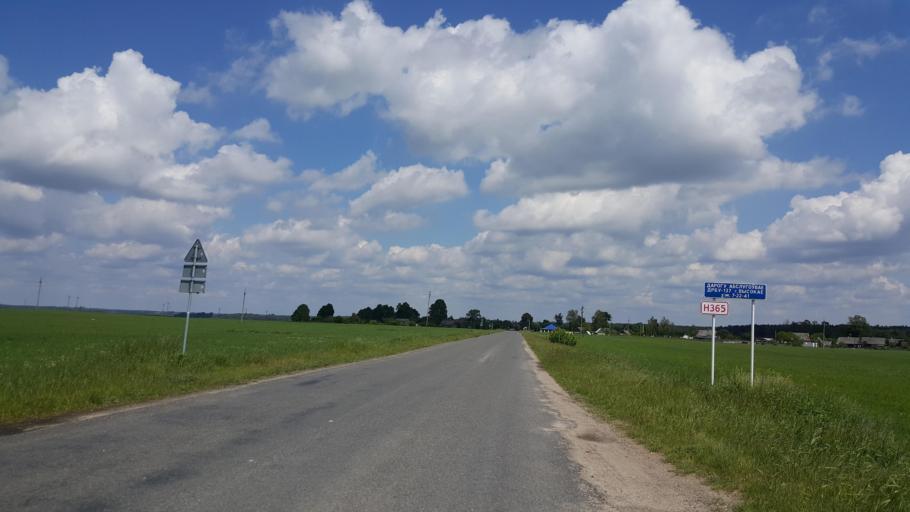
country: BY
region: Brest
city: Kamyanyets
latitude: 52.4000
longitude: 23.8861
